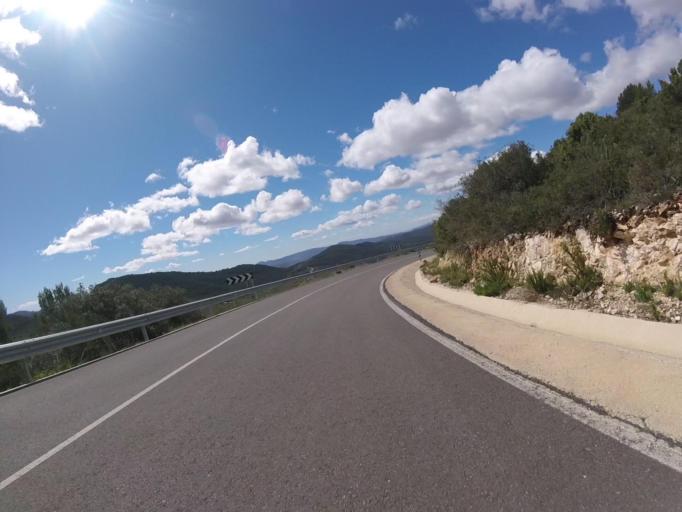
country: ES
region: Valencia
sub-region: Provincia de Castello
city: Culla
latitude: 40.2958
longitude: -0.1175
